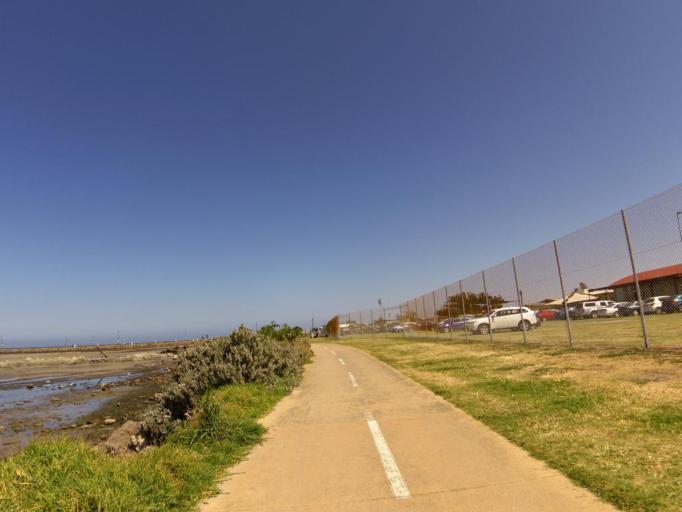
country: AU
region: Victoria
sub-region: Hobsons Bay
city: Seaholme
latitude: -37.8643
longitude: 144.8497
